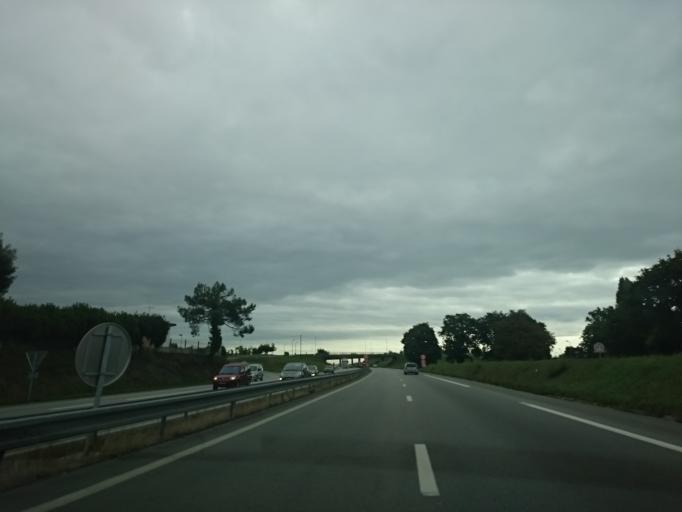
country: FR
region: Brittany
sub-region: Departement du Morbihan
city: Plescop
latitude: 47.6609
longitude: -2.7993
